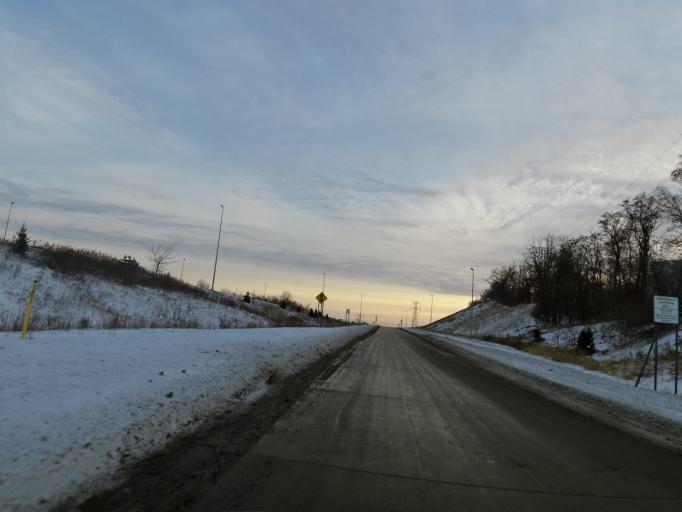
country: US
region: Minnesota
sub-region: Hennepin County
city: Hopkins
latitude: 44.8910
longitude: -93.4443
